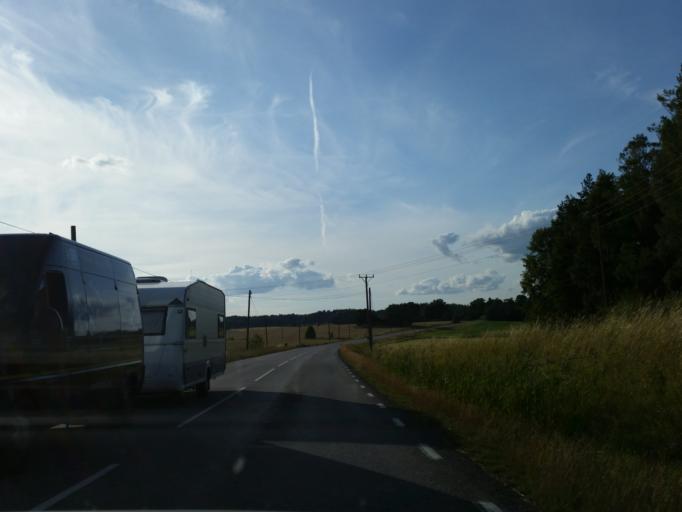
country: SE
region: Stockholm
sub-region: Sodertalje Kommun
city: Molnbo
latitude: 58.9934
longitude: 17.4156
